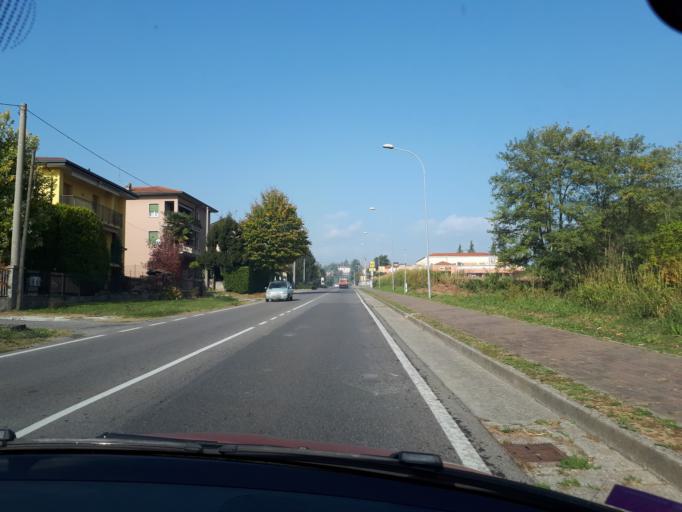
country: IT
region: Lombardy
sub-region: Provincia di Lecco
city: Casatenovo
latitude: 45.6864
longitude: 9.3164
